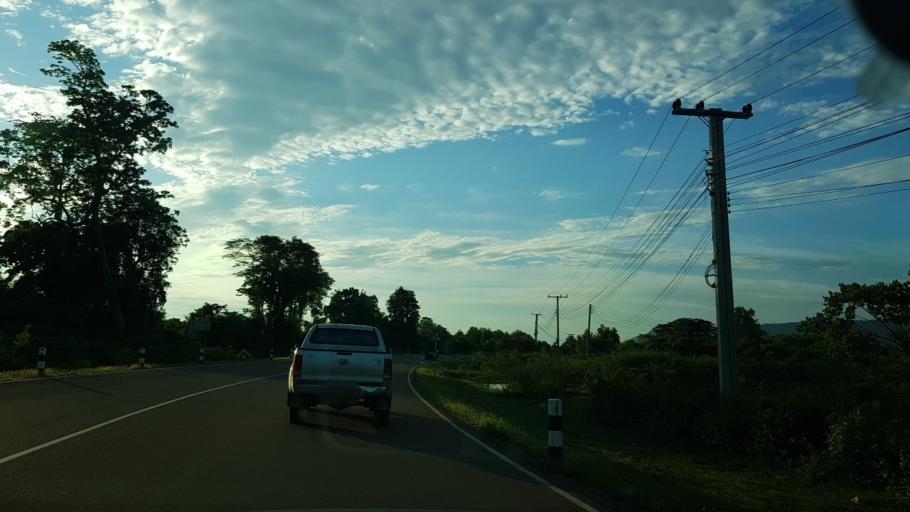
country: TH
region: Nong Khai
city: Sangkhom
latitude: 18.0861
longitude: 102.2917
